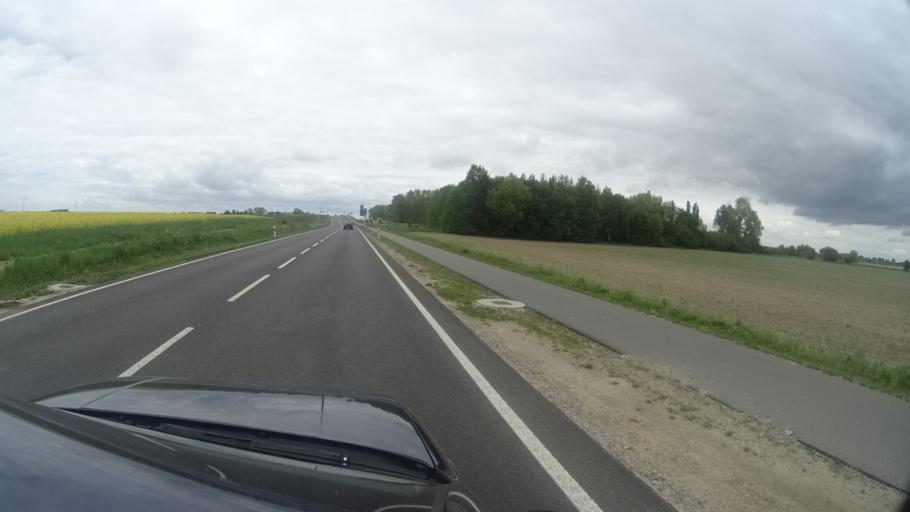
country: DE
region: Brandenburg
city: Fehrbellin
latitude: 52.8447
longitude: 12.7774
